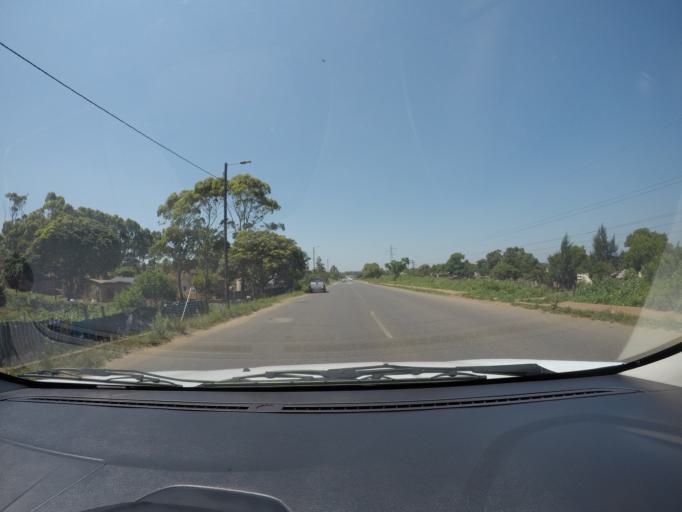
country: ZA
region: KwaZulu-Natal
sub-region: uThungulu District Municipality
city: eSikhawini
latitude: -28.8346
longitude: 31.9391
